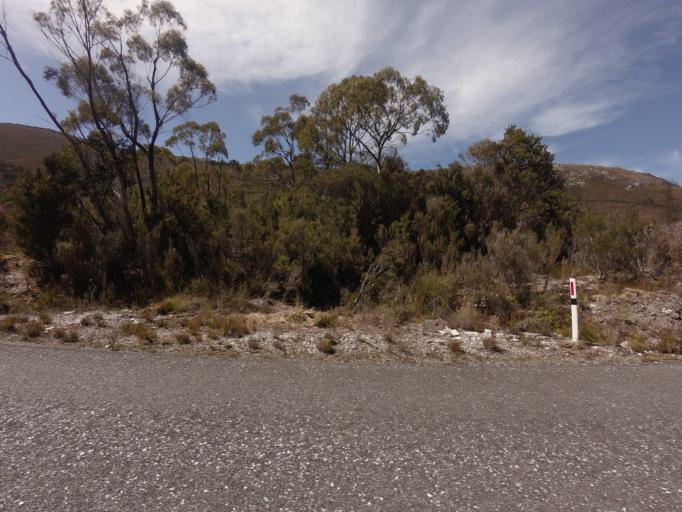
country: AU
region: Tasmania
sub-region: West Coast
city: Queenstown
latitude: -42.7869
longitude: 146.0623
